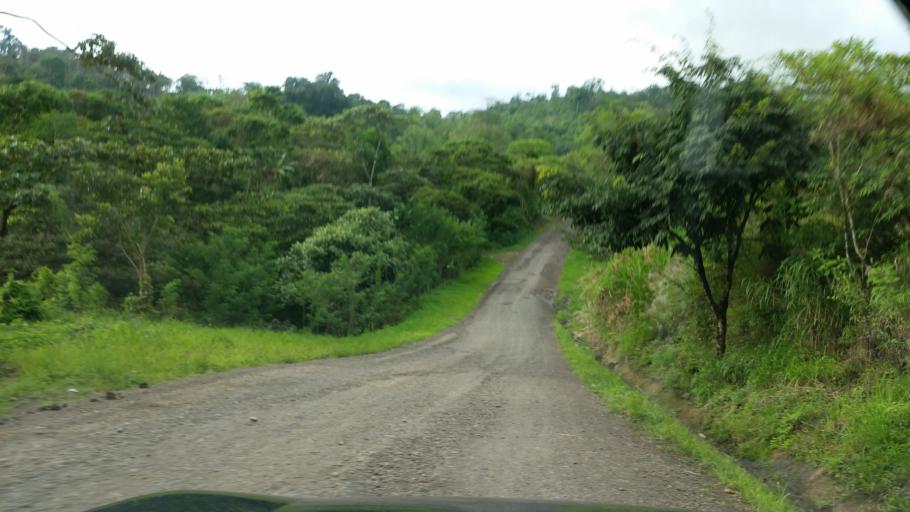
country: NI
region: Jinotega
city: Jinotega
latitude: 13.2585
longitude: -85.7388
